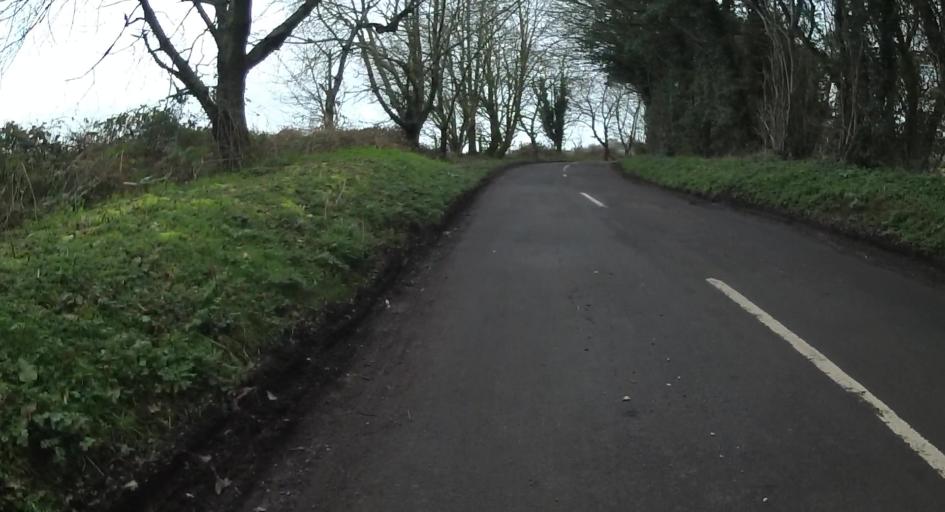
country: GB
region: England
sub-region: Hampshire
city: Kingsclere
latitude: 51.2841
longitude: -1.2257
